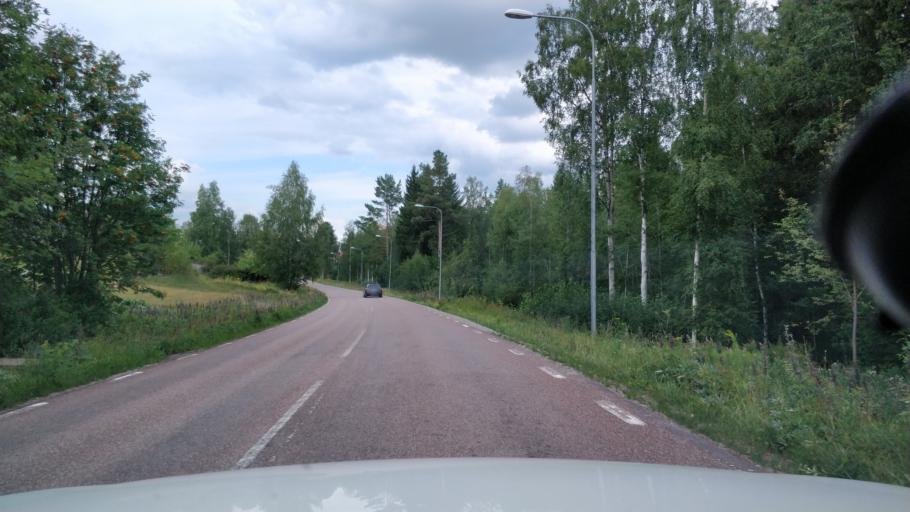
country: SE
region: Dalarna
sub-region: Faluns Kommun
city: Bjursas
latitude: 60.7425
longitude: 15.4684
